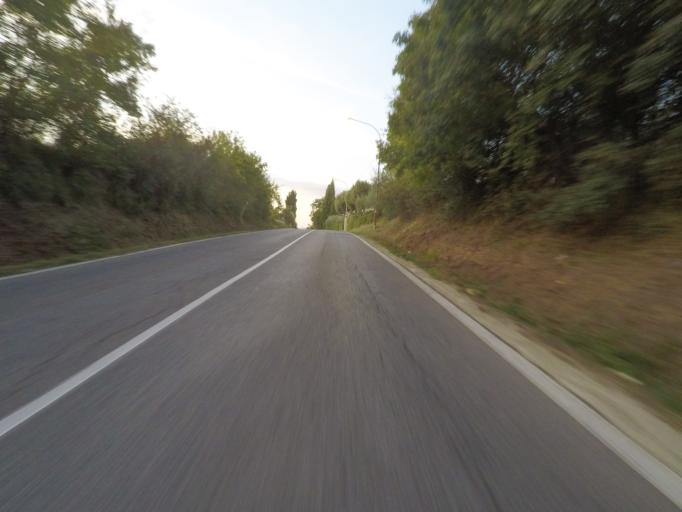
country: IT
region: Tuscany
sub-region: Provincia di Siena
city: Torrita di Siena
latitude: 43.1744
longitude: 11.7737
